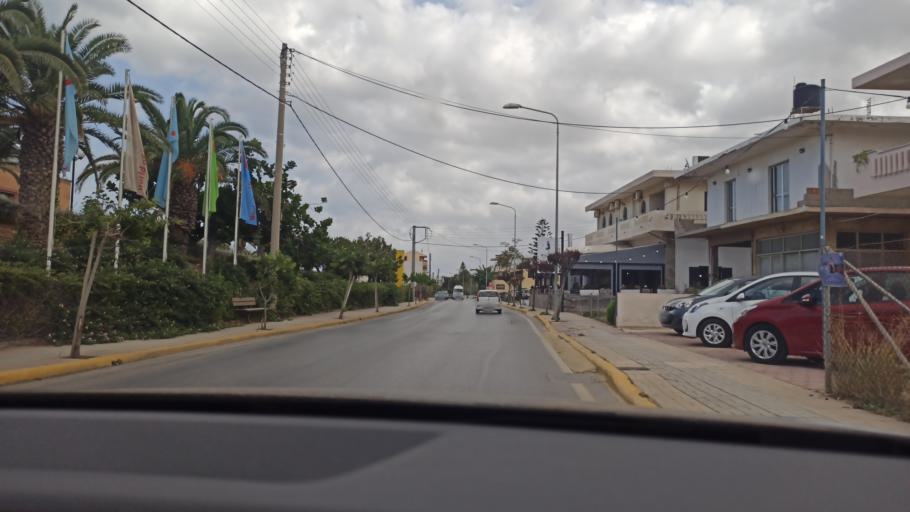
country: GR
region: Crete
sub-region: Nomos Irakleiou
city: Gazi
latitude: 35.3355
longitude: 25.0845
